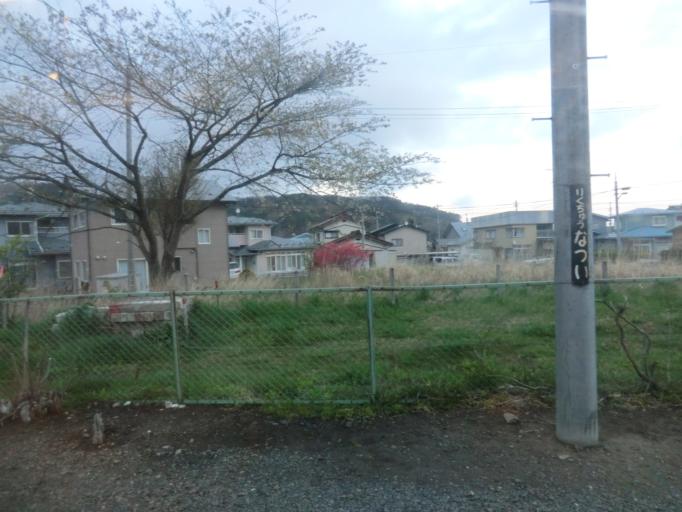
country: JP
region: Aomori
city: Hachinohe
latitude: 40.2079
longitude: 141.7920
